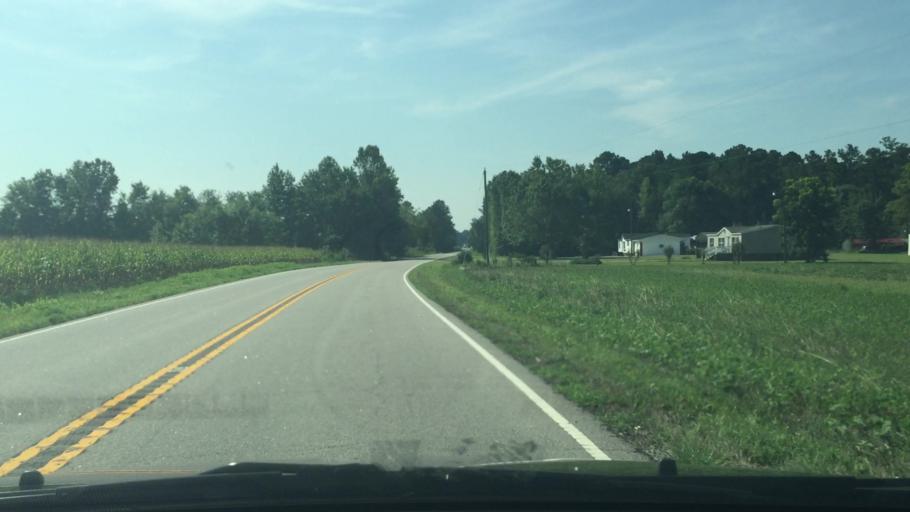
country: US
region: Virginia
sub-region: Southampton County
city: Courtland
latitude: 36.8370
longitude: -77.1290
